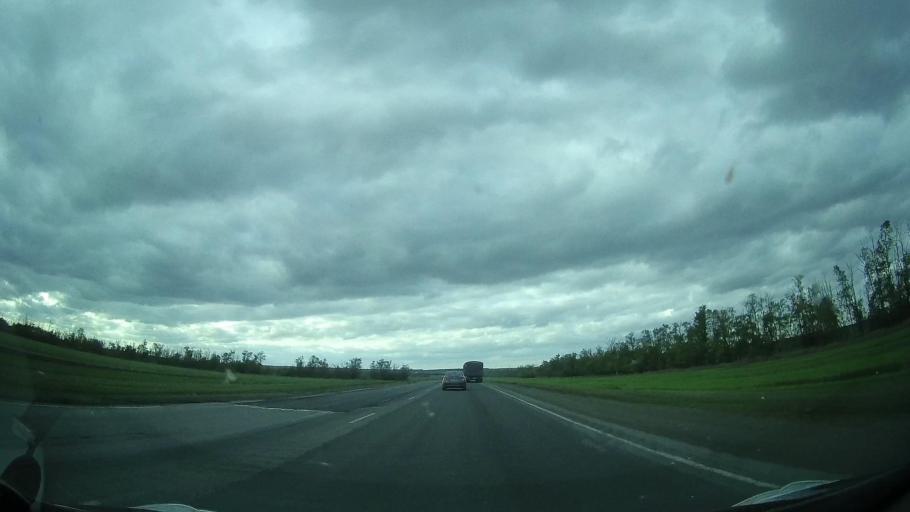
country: RU
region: Rostov
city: Kagal'nitskaya
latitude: 46.8628
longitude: 40.1820
